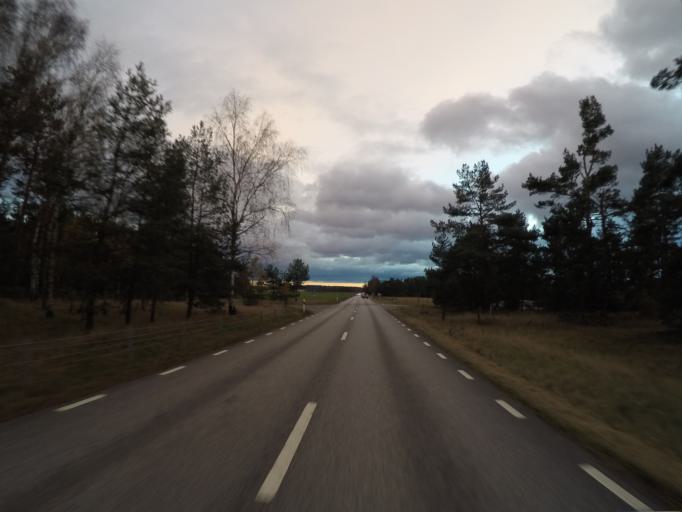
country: SE
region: Skane
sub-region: Kristianstads Kommun
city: Norra Asum
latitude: 55.9311
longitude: 14.0751
